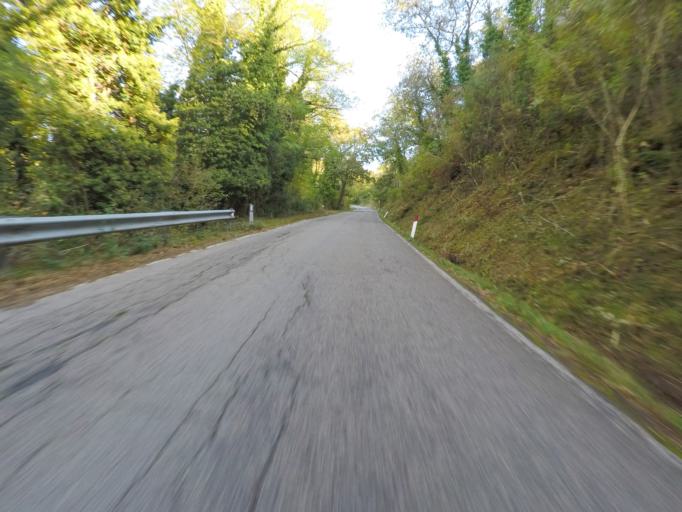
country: IT
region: Tuscany
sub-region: Provincia di Siena
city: Radda in Chianti
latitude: 43.4664
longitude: 11.3781
